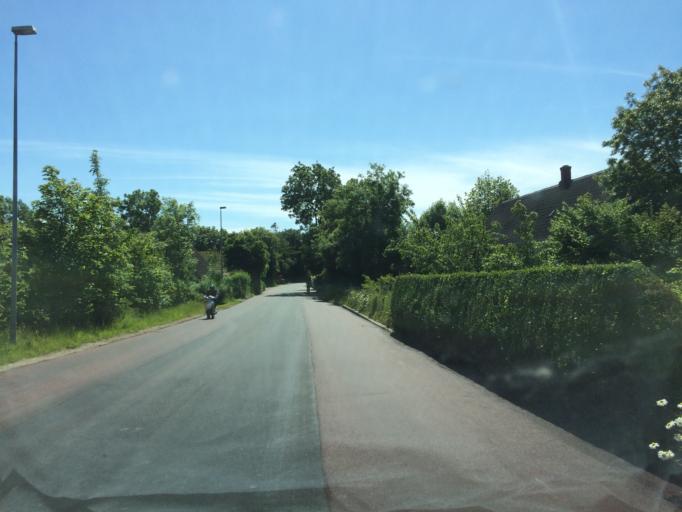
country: DK
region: Central Jutland
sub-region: Samso Kommune
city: Tranebjerg
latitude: 55.8182
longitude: 10.6054
